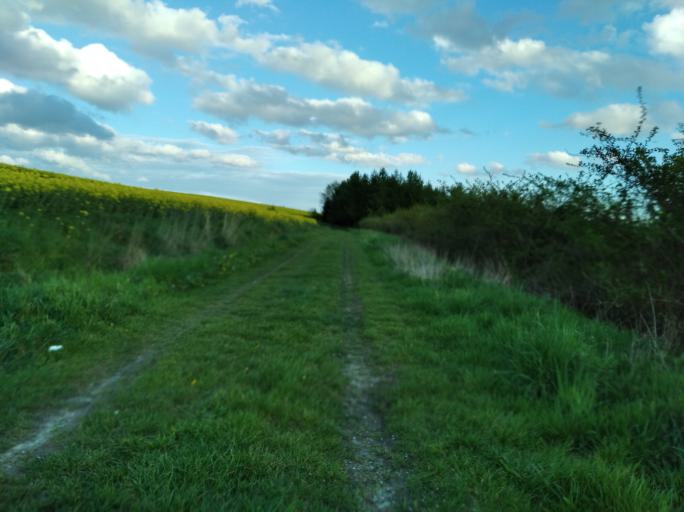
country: PL
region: Subcarpathian Voivodeship
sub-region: Powiat strzyzowski
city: Wysoka Strzyzowska
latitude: 49.8600
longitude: 21.7566
